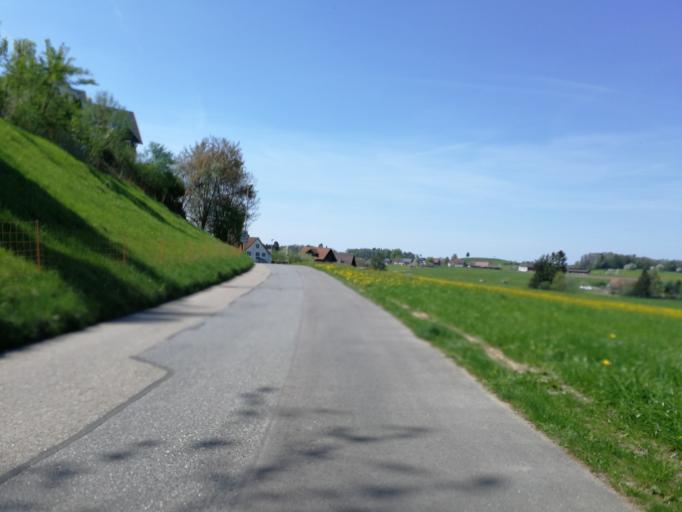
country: CH
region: Zurich
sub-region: Bezirk Hinwil
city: Bubikon
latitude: 47.2695
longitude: 8.8144
